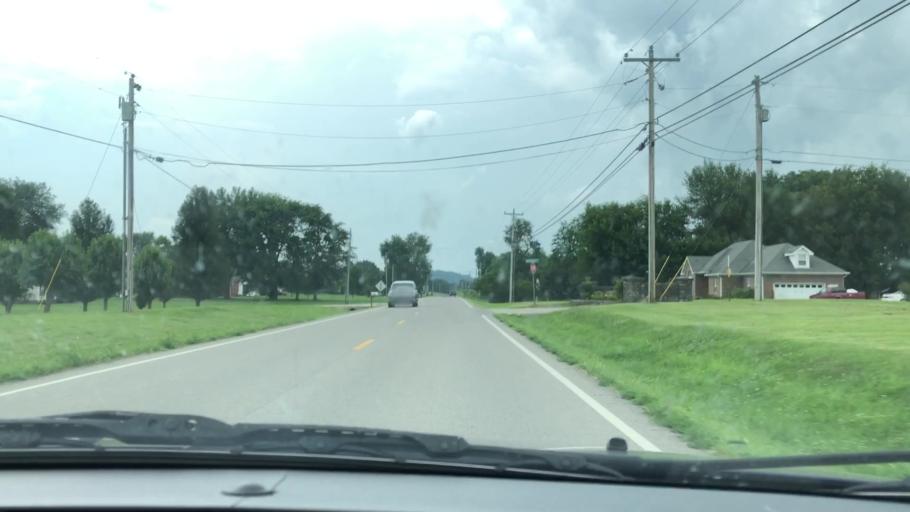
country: US
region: Tennessee
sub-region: Maury County
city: Spring Hill
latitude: 35.7681
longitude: -87.0067
